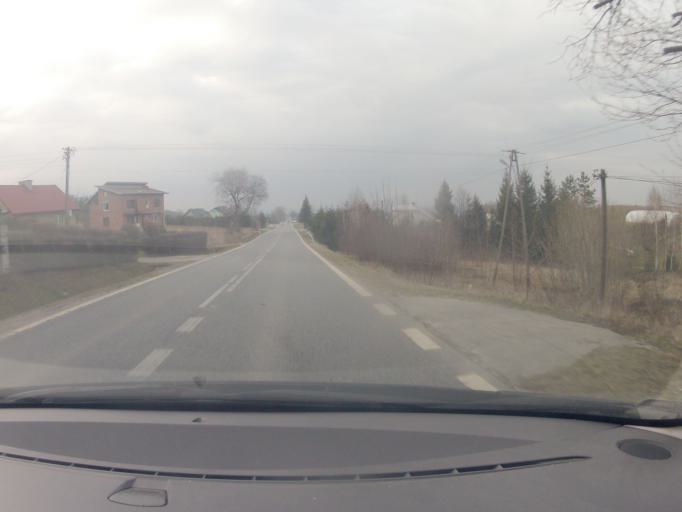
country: PL
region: Subcarpathian Voivodeship
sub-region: Powiat jasielski
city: Nowy Zmigrod
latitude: 49.5746
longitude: 21.5632
